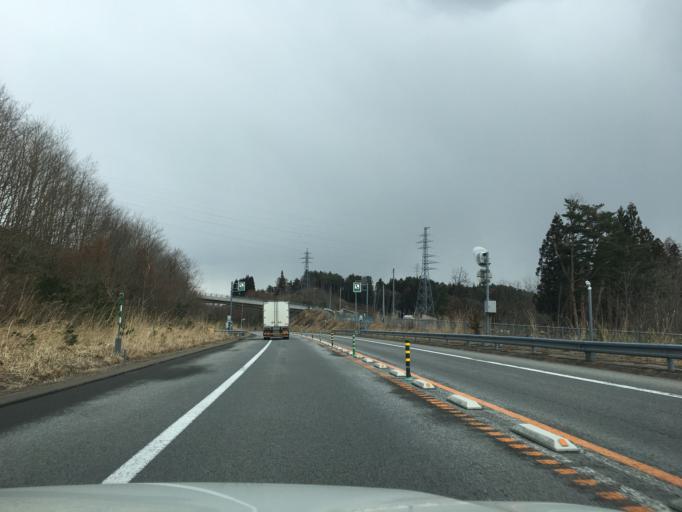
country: JP
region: Aomori
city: Aomori Shi
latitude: 40.8000
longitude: 140.6993
